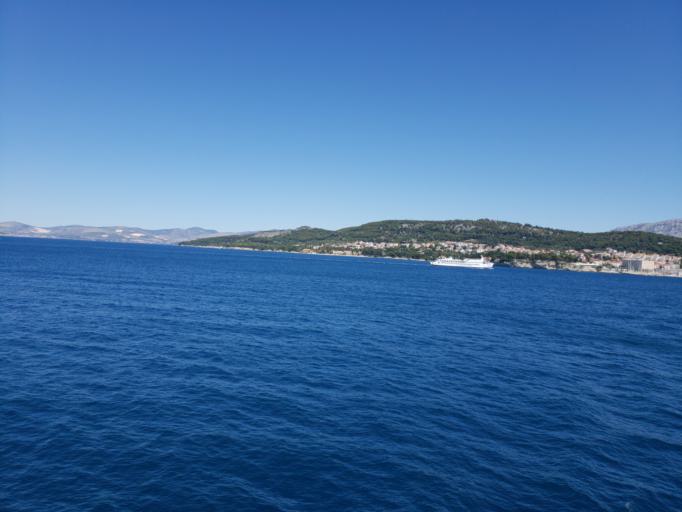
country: HR
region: Splitsko-Dalmatinska
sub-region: Grad Split
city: Split
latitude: 43.4914
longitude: 16.4330
